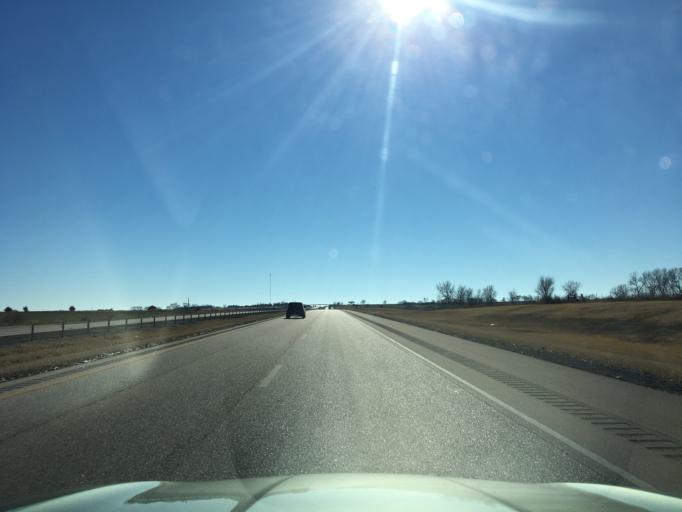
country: US
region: Oklahoma
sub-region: Kay County
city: Blackwell
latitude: 36.8828
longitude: -97.3517
